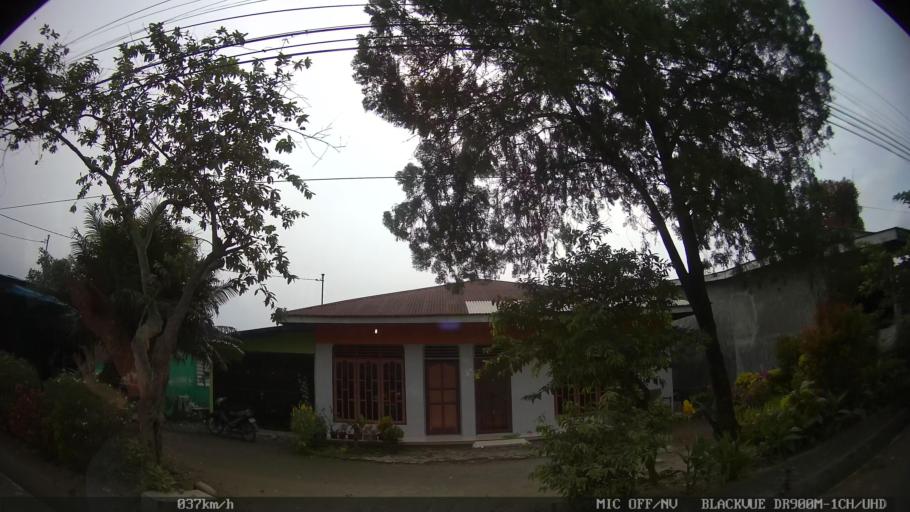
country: ID
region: North Sumatra
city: Medan
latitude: 3.5713
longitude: 98.7565
